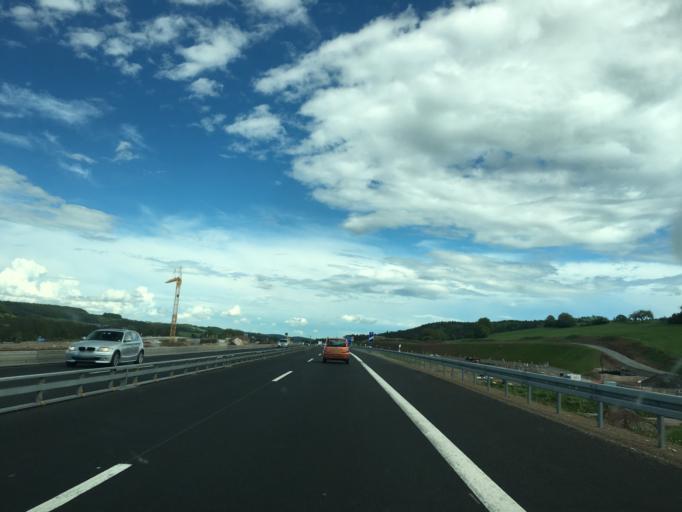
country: DE
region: Bavaria
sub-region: Regierungsbezirk Unterfranken
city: Geiselwind
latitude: 49.7700
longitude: 10.4730
